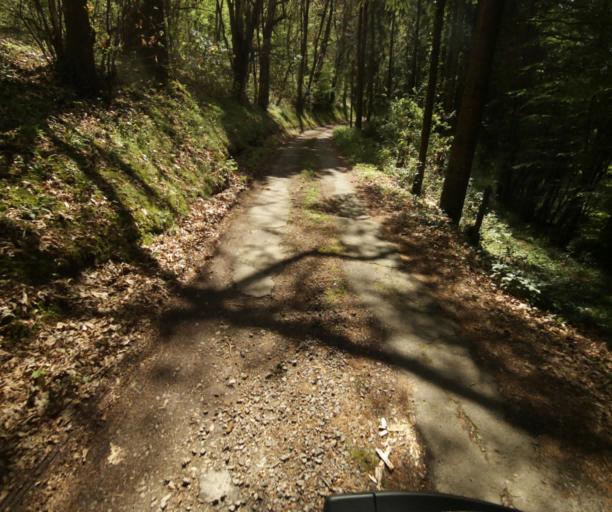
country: FR
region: Limousin
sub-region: Departement de la Correze
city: Naves
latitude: 45.2911
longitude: 1.7761
